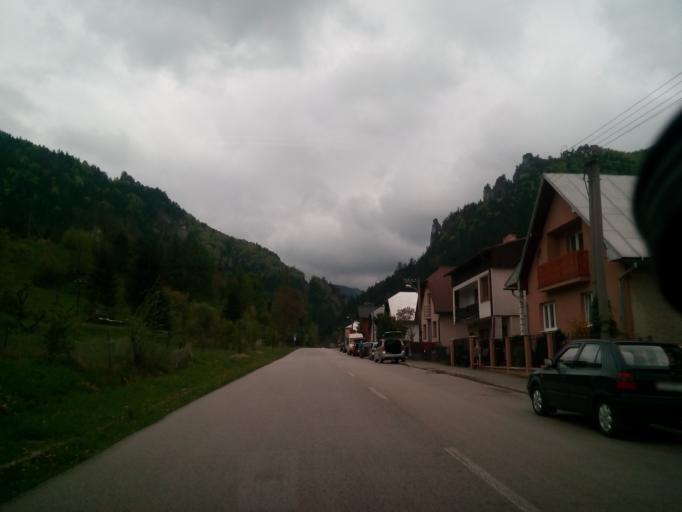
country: SK
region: Zilinsky
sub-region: Okres Zilina
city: Terchova
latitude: 49.2541
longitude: 19.0366
